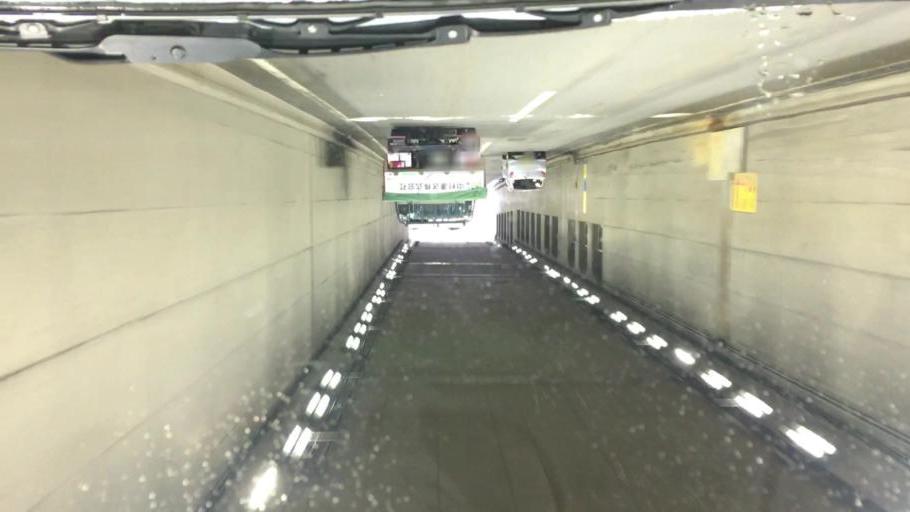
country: JP
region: Hokkaido
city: Sapporo
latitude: 43.0695
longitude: 141.3810
